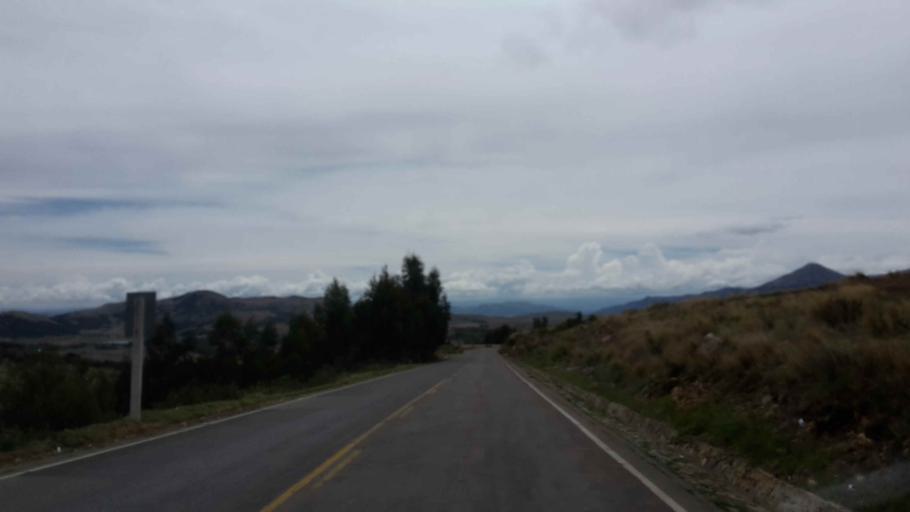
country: BO
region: Cochabamba
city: Arani
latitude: -17.4613
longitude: -65.6788
